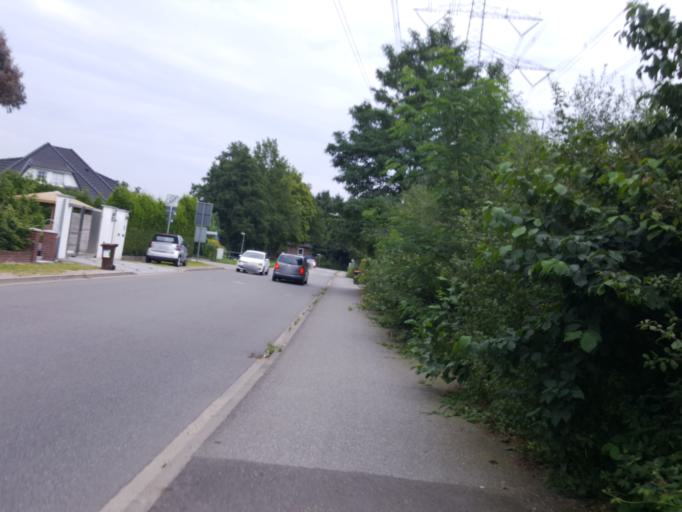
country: DE
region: Schleswig-Holstein
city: Oststeinbek
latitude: 53.5203
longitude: 10.1662
